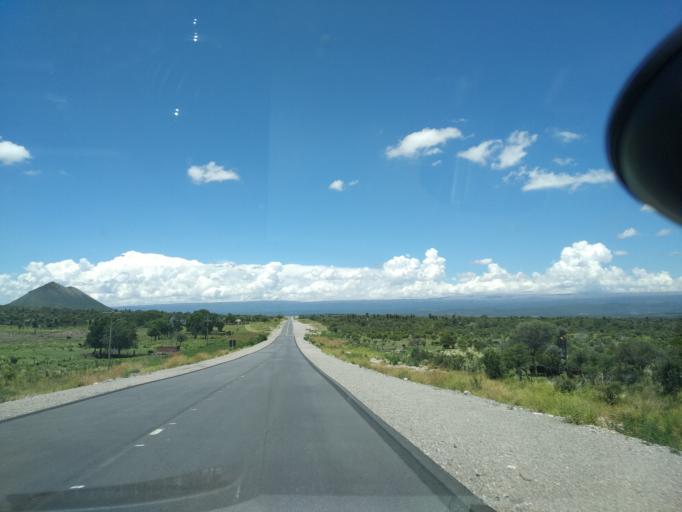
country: AR
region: Cordoba
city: Salsacate
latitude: -31.3618
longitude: -65.1916
